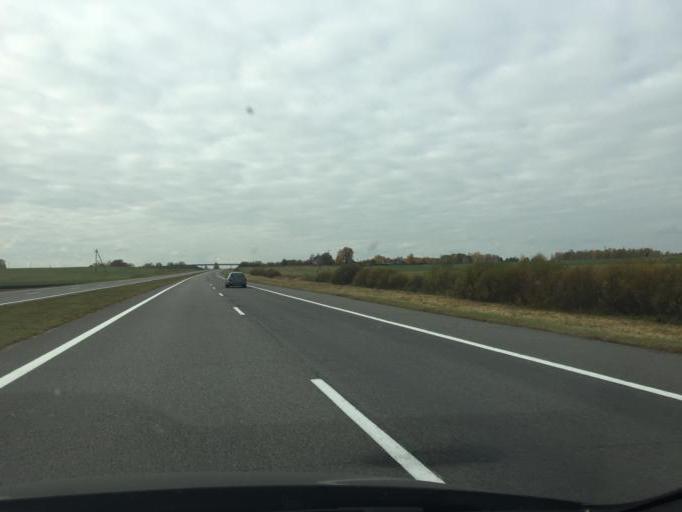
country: BY
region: Minsk
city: Stan'kava
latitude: 53.6758
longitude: 27.2230
